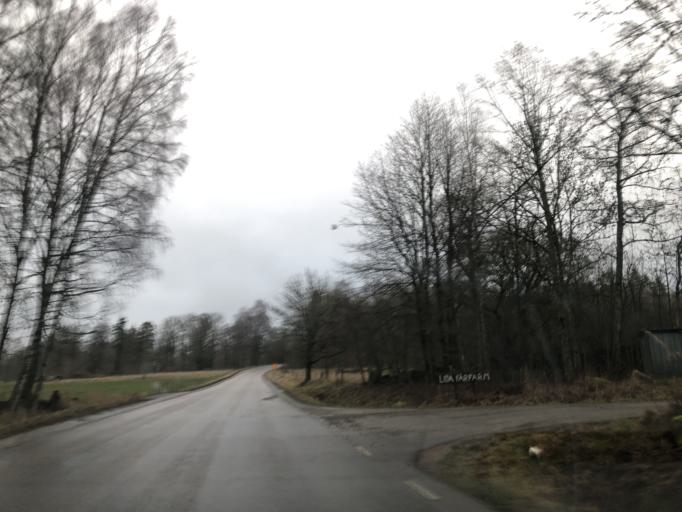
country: SE
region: Vaestra Goetaland
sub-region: Ulricehamns Kommun
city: Ulricehamn
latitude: 57.8339
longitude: 13.3172
